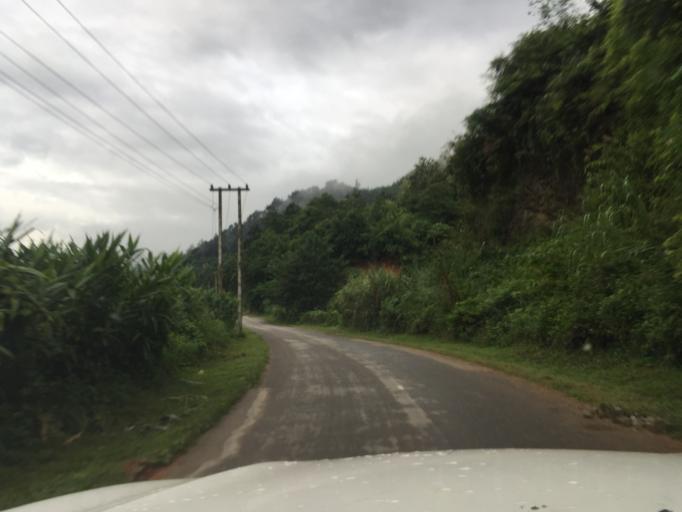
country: LA
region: Oudomxai
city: Muang La
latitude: 20.9132
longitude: 102.1903
